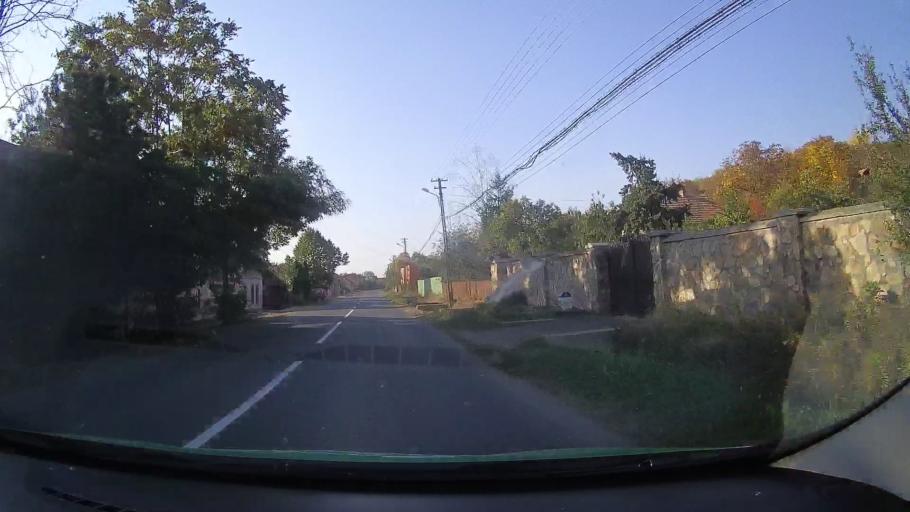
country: RO
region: Arad
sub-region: Comuna Ghioroc
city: Ghioroc
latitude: 46.1450
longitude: 21.5992
